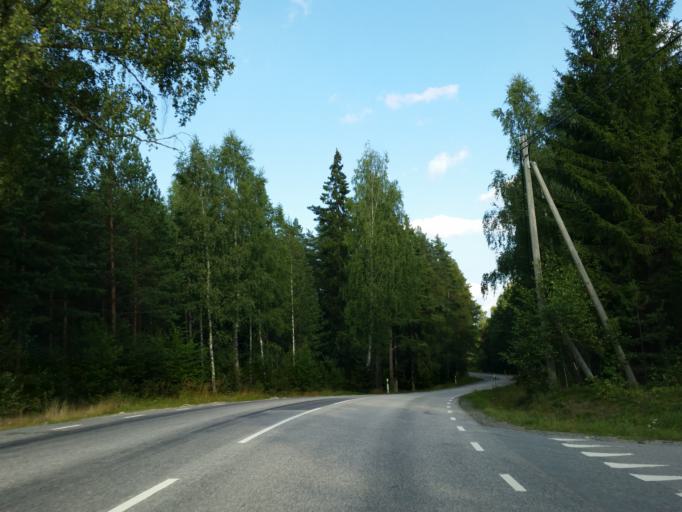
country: SE
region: Stockholm
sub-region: Nykvarns Kommun
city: Nykvarn
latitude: 59.2068
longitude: 17.3851
